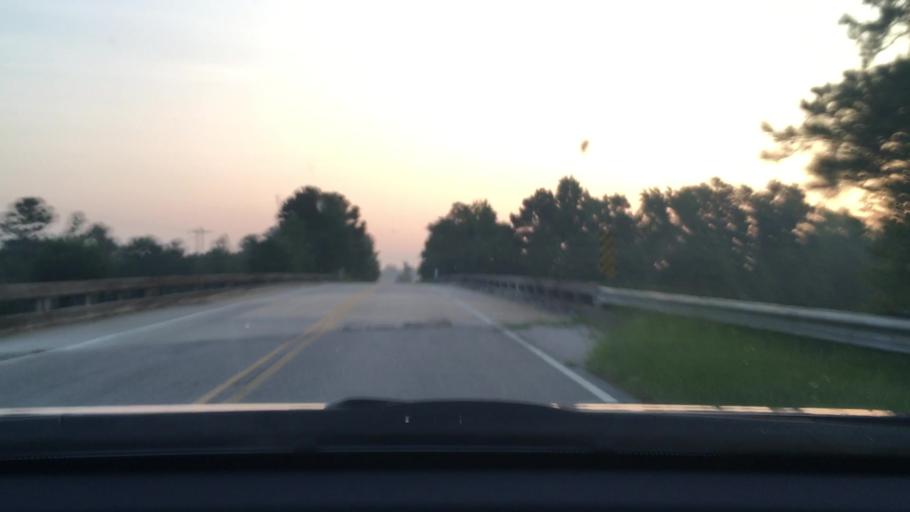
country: US
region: South Carolina
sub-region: Lee County
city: Bishopville
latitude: 34.1937
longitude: -80.1403
